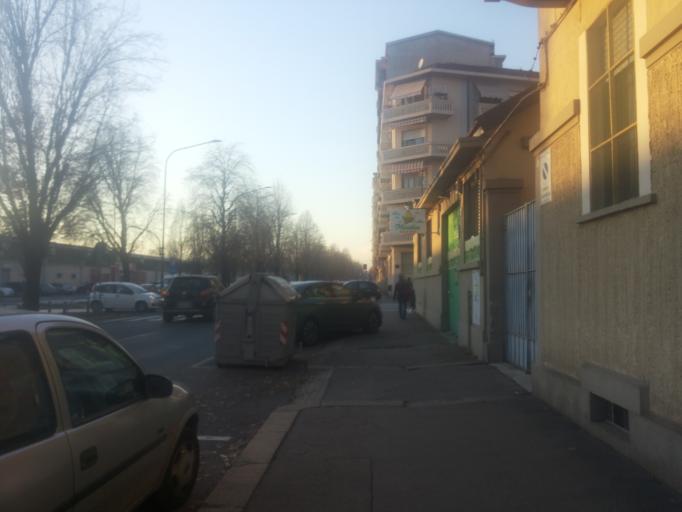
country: IT
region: Piedmont
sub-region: Provincia di Torino
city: Lesna
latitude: 45.0563
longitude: 7.6425
